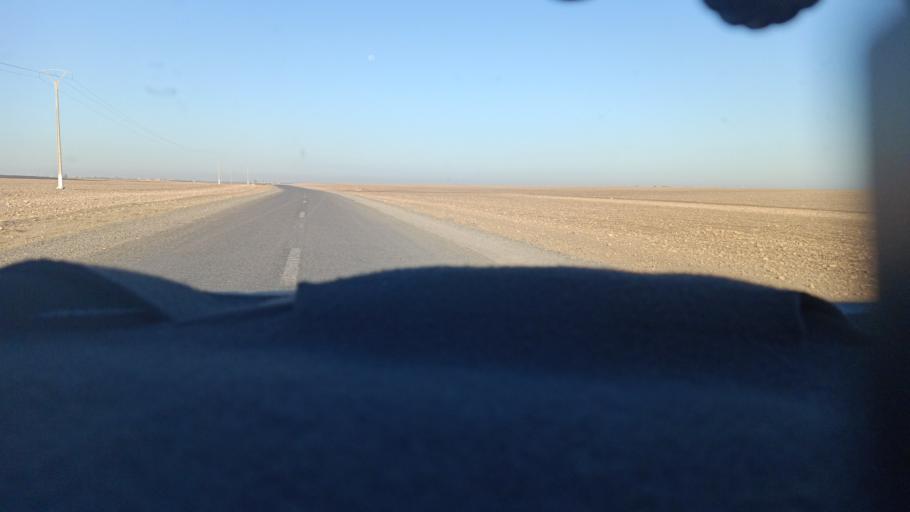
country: MA
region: Doukkala-Abda
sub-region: Safi
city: Youssoufia
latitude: 32.3712
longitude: -8.6836
